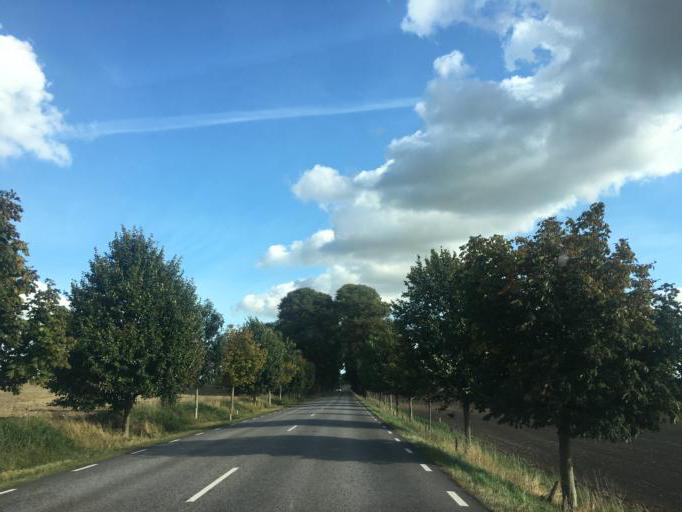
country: SE
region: Skane
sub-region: Eslovs Kommun
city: Eslov
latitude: 55.7790
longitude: 13.2961
